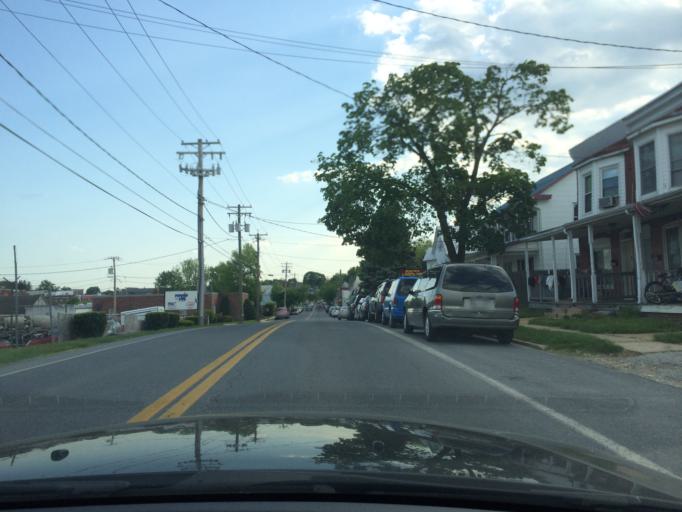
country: US
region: Maryland
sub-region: Carroll County
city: Westminster
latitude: 39.5793
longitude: -76.9936
